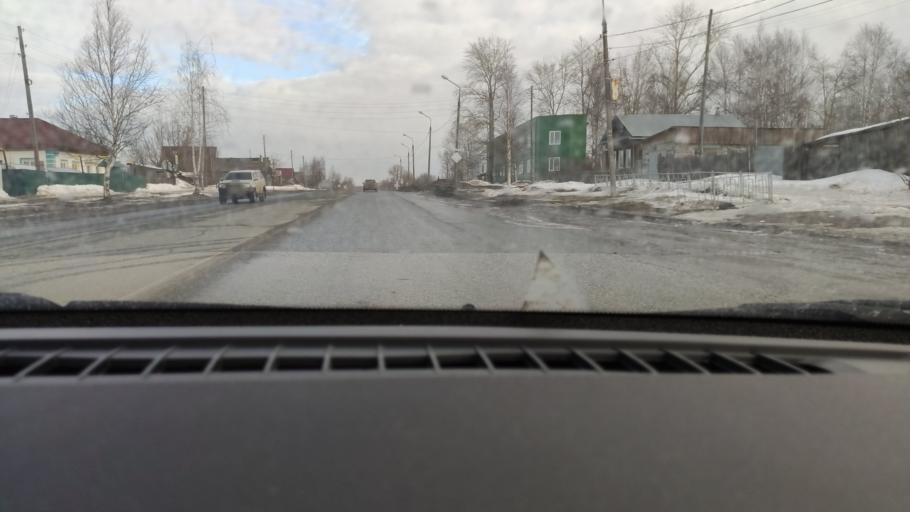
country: RU
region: Perm
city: Polazna
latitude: 58.1148
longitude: 56.4009
